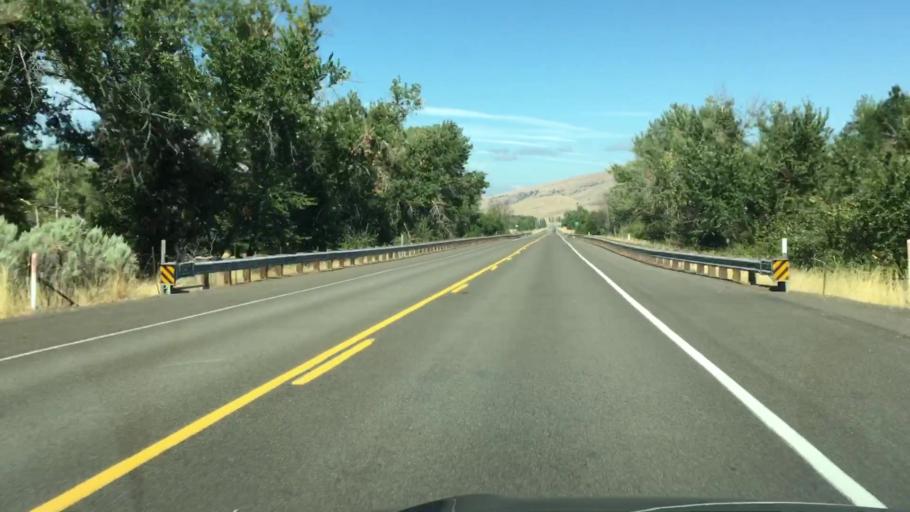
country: US
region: Oregon
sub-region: Wasco County
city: The Dalles
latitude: 45.2401
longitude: -121.1499
